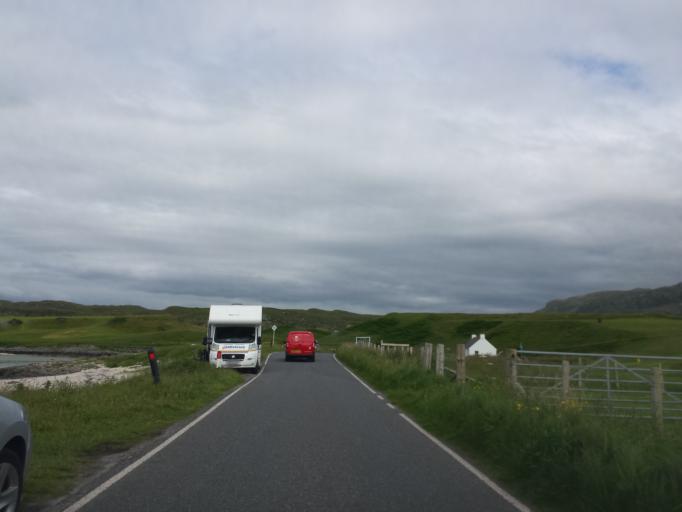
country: GB
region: Scotland
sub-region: Argyll and Bute
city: Isle Of Mull
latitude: 56.9397
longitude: -5.8562
